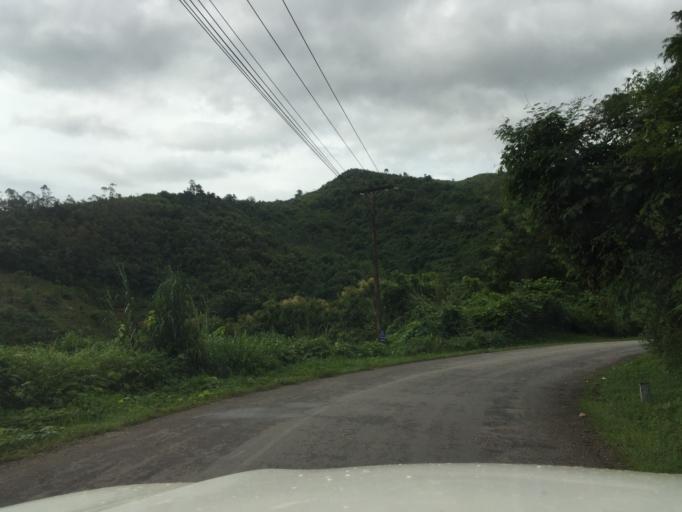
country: LA
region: Oudomxai
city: Muang La
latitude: 20.7920
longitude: 102.0852
